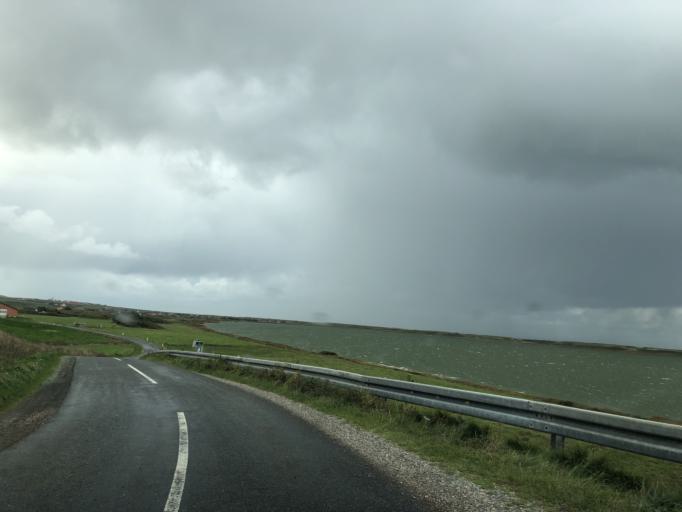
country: DK
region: Central Jutland
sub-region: Lemvig Kommune
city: Harboore
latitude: 56.5477
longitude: 8.1406
